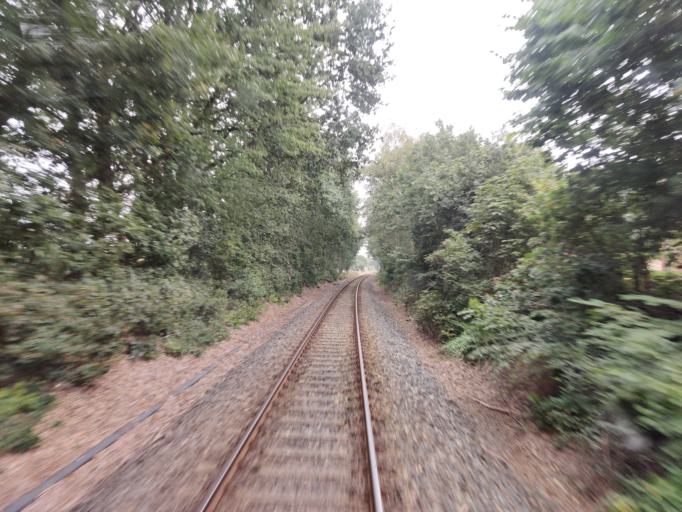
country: DE
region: Lower Saxony
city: Kutenholz
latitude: 53.4887
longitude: 9.2680
